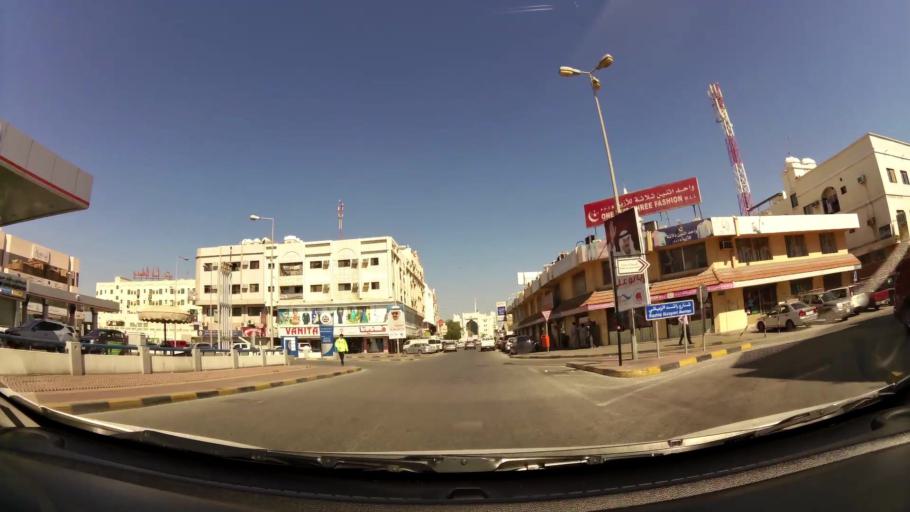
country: BH
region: Muharraq
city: Al Muharraq
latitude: 26.2477
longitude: 50.6091
